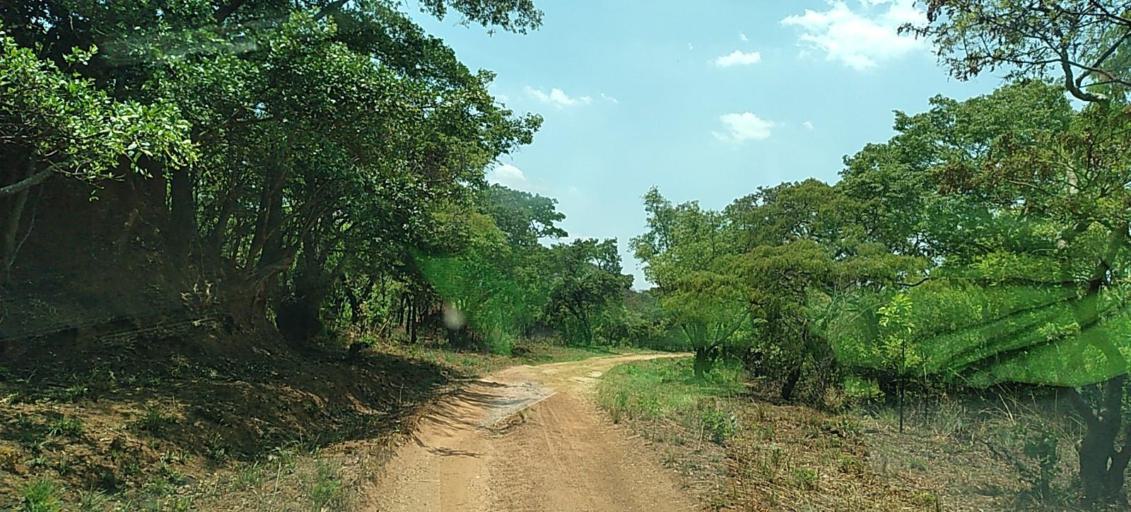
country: CD
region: Katanga
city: Kolwezi
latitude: -11.3627
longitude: 25.2064
